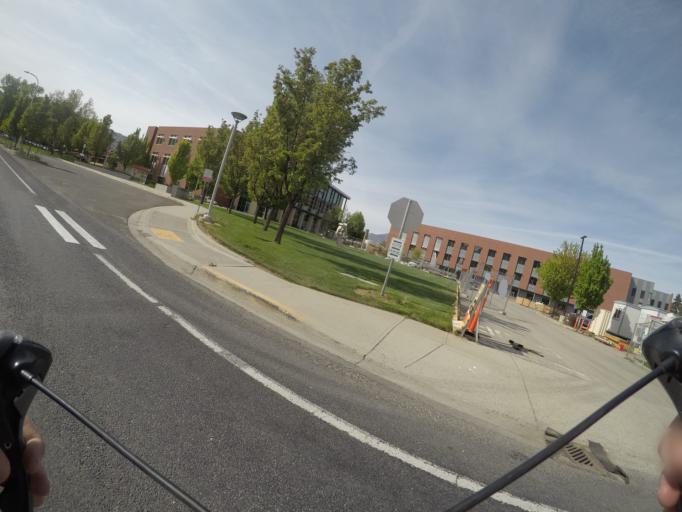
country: US
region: Washington
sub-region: Chelan County
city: West Wenatchee
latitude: 47.4299
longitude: -120.3354
